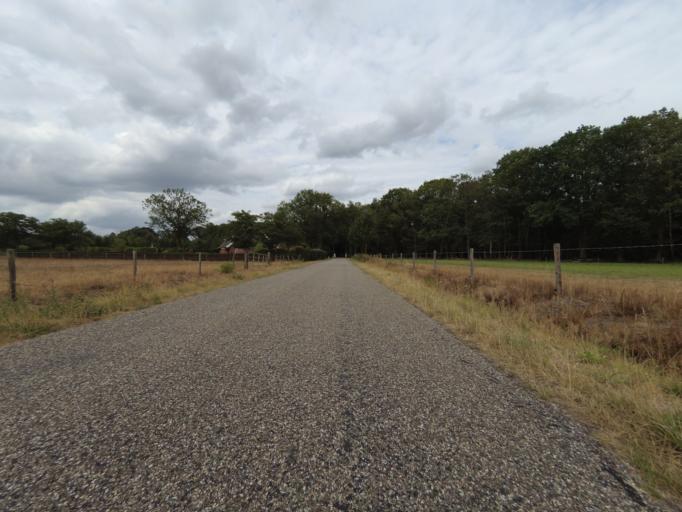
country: NL
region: Overijssel
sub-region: Gemeente Enschede
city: Enschede
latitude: 52.2383
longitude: 6.9286
